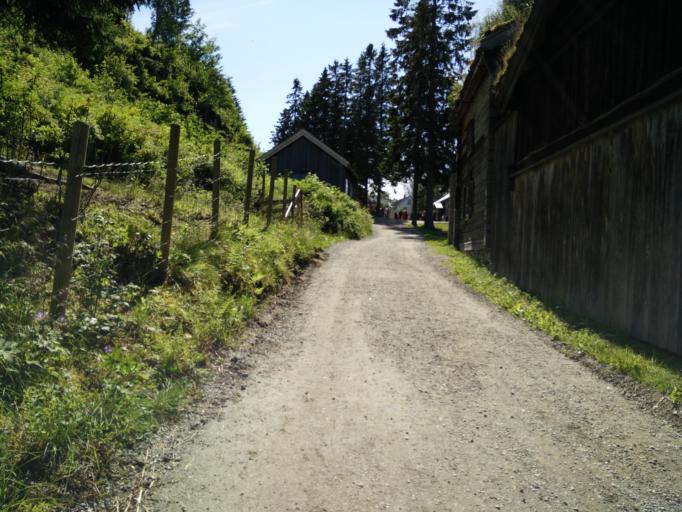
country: NO
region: Sor-Trondelag
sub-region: Trondheim
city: Trondheim
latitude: 63.4203
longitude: 10.3563
